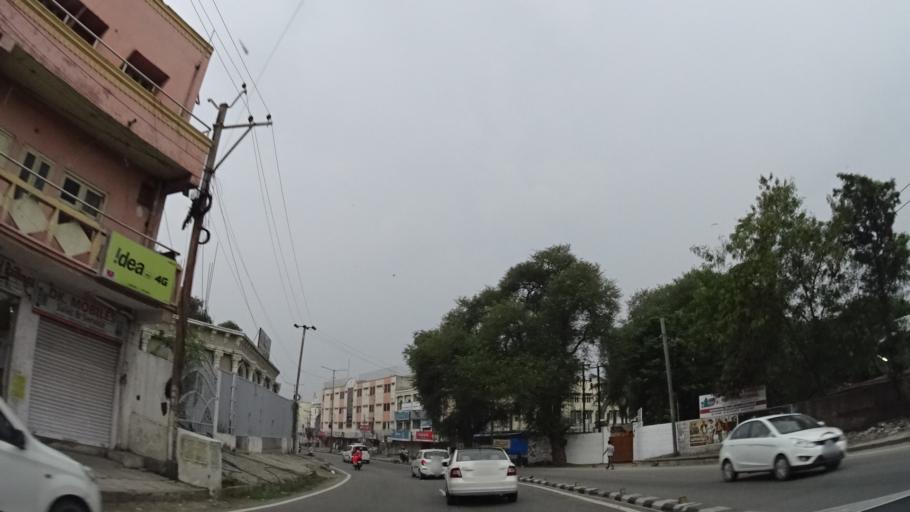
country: IN
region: Telangana
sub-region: Rangareddi
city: Quthbullapur
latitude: 17.4600
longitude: 78.4759
